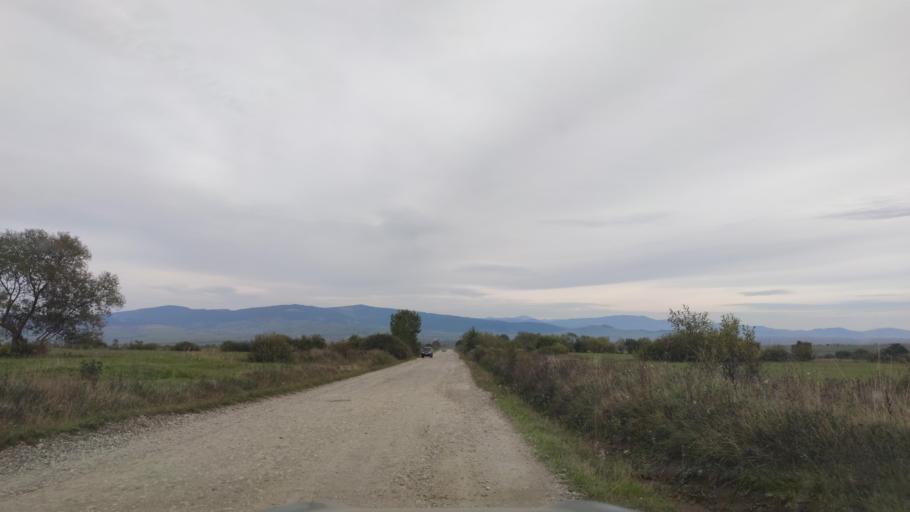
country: RO
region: Harghita
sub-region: Comuna Remetea
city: Remetea
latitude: 46.8104
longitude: 25.3935
